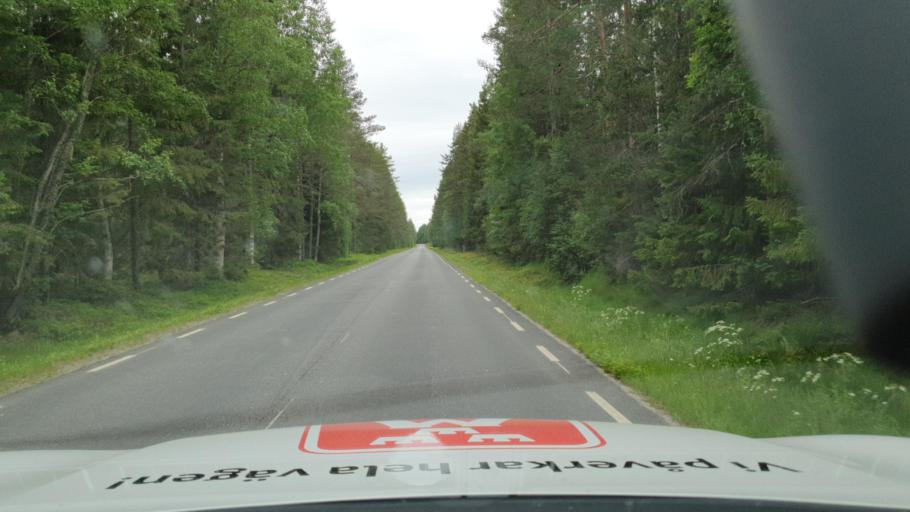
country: SE
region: Vaesterbotten
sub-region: Nordmalings Kommun
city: Nordmaling
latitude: 63.7211
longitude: 19.5509
